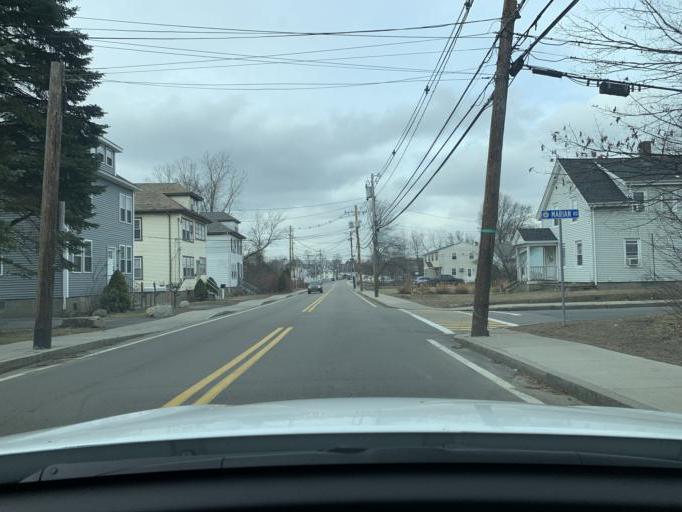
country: US
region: Massachusetts
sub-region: Middlesex County
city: Framingham
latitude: 42.2751
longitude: -71.4042
